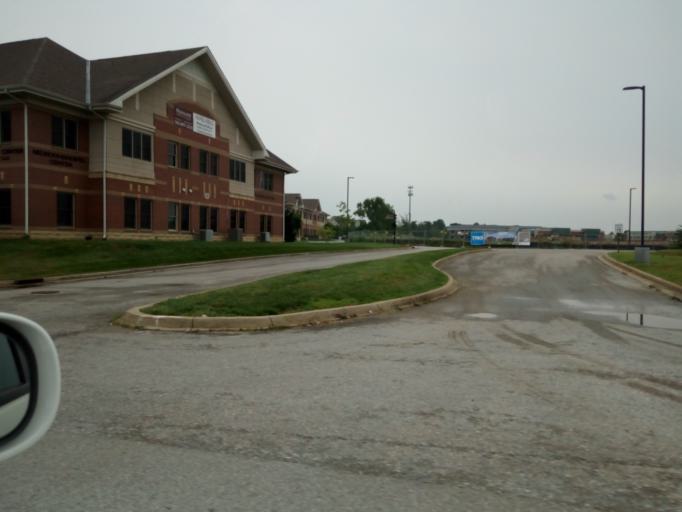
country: US
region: Kentucky
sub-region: Oldham County
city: Pewee Valley
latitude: 38.2734
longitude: -85.4890
